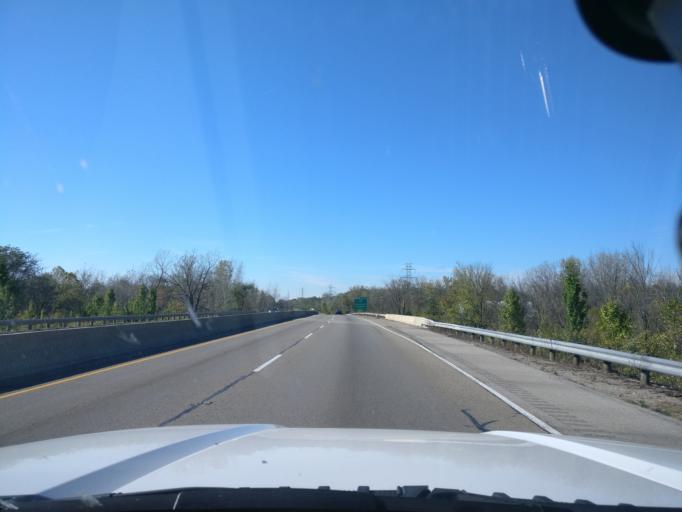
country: US
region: Ohio
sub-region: Greene County
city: Beavercreek
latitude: 39.7262
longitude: -84.0668
